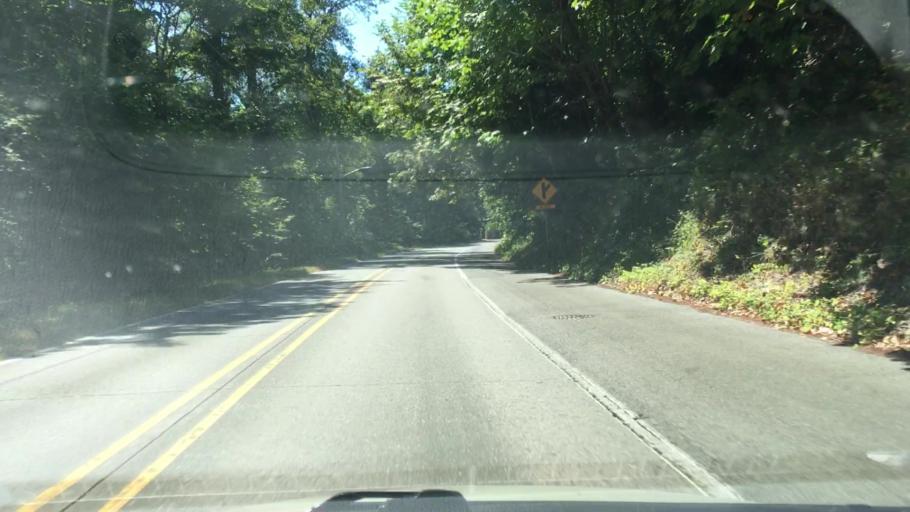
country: US
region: Washington
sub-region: King County
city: Sammamish
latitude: 47.6224
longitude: -122.0917
